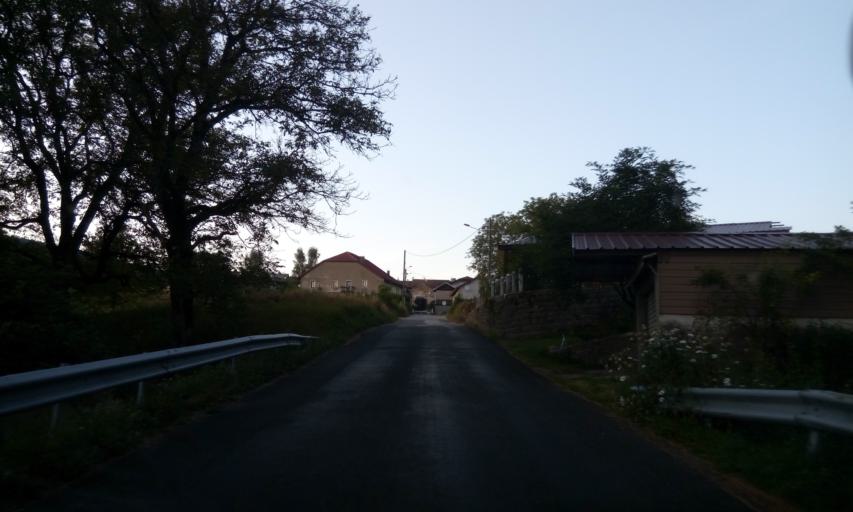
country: FR
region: Rhone-Alpes
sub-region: Departement de l'Ain
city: Nantua
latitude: 46.1805
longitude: 5.6853
